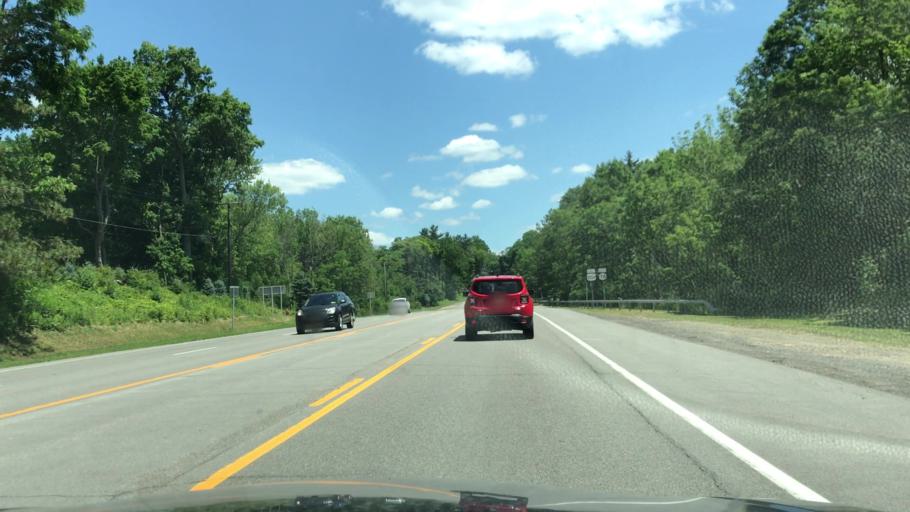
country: US
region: New York
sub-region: Erie County
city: East Aurora
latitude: 42.7675
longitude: -78.5915
